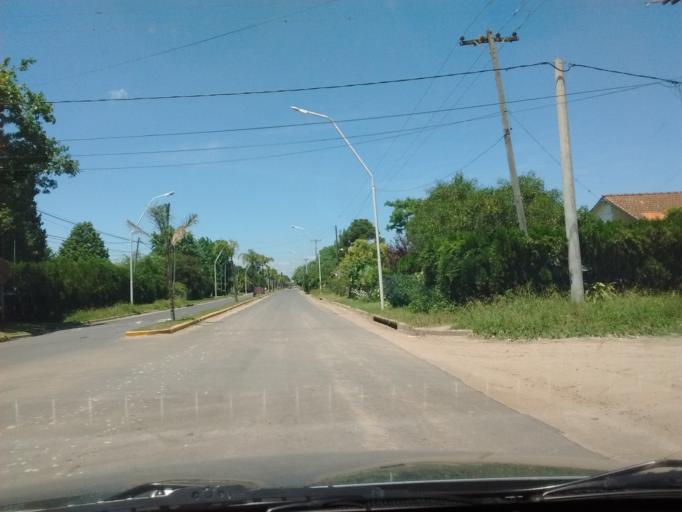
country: AR
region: Entre Rios
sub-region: Departamento de Gualeguay
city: Gualeguay
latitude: -33.1289
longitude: -59.3227
